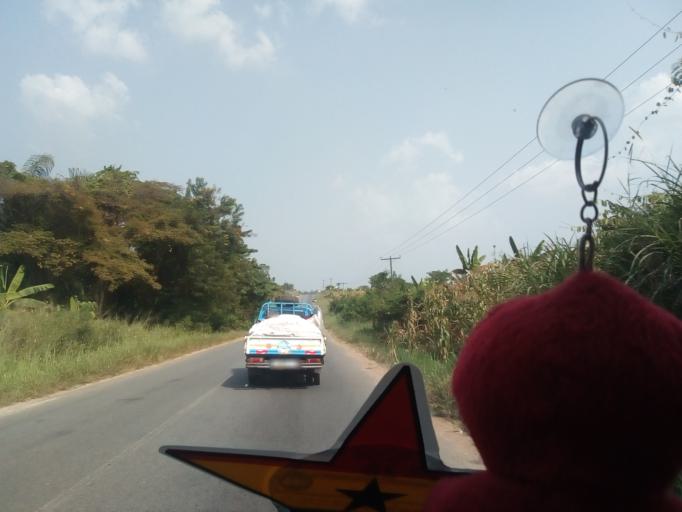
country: GH
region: Eastern
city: Suhum
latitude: 6.0443
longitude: -0.4218
